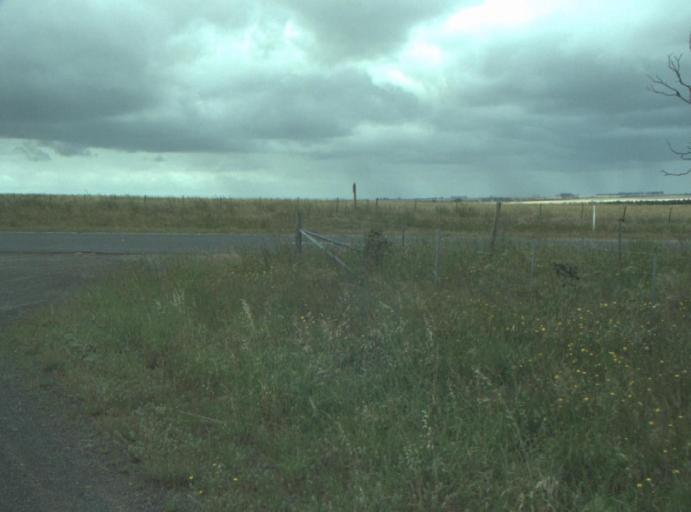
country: AU
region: Victoria
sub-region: Greater Geelong
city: Lara
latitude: -37.8917
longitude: 144.3505
